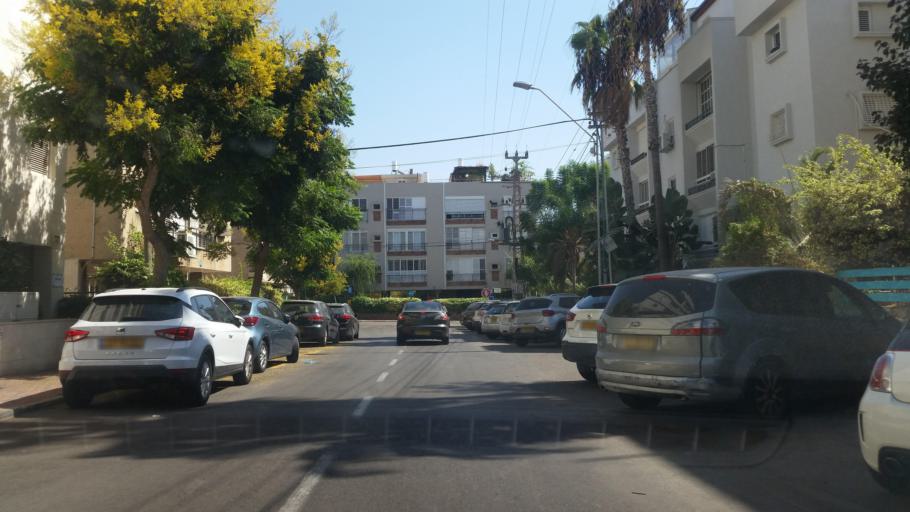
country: IL
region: Central District
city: Ra'anana
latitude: 32.1768
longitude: 34.8768
